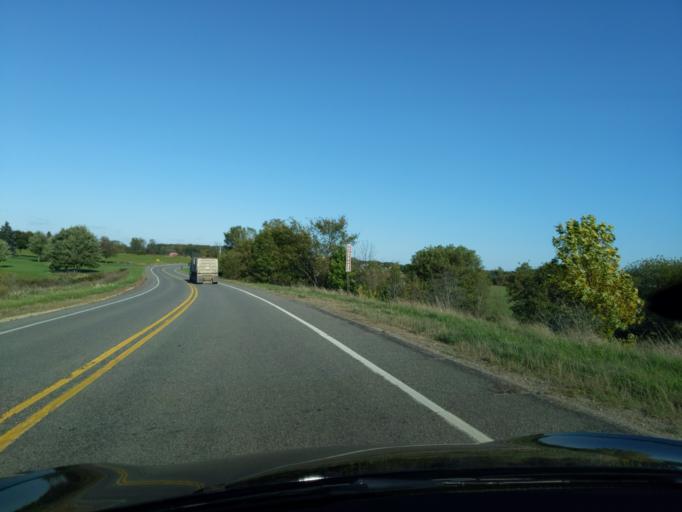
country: US
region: Michigan
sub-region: Clinton County
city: Saint Johns
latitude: 42.9290
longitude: -84.5133
